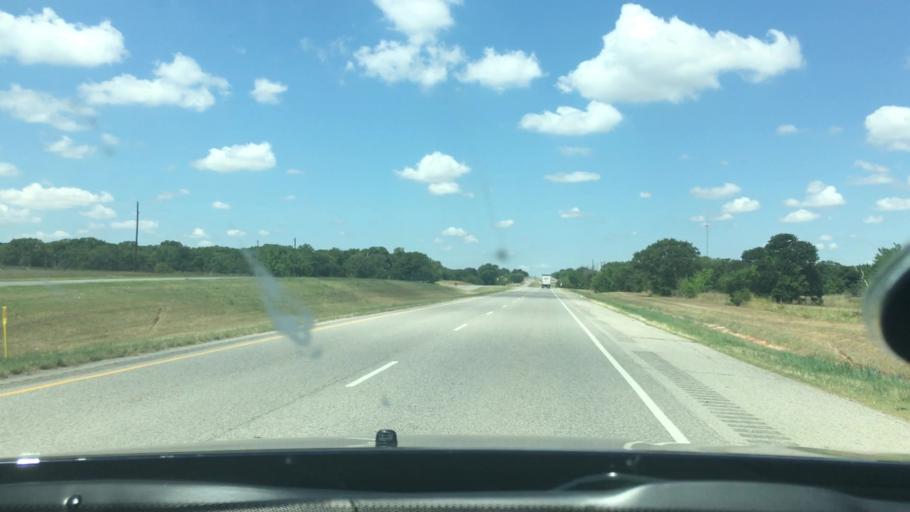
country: US
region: Oklahoma
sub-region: Carter County
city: Wilson
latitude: 34.1730
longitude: -97.3904
